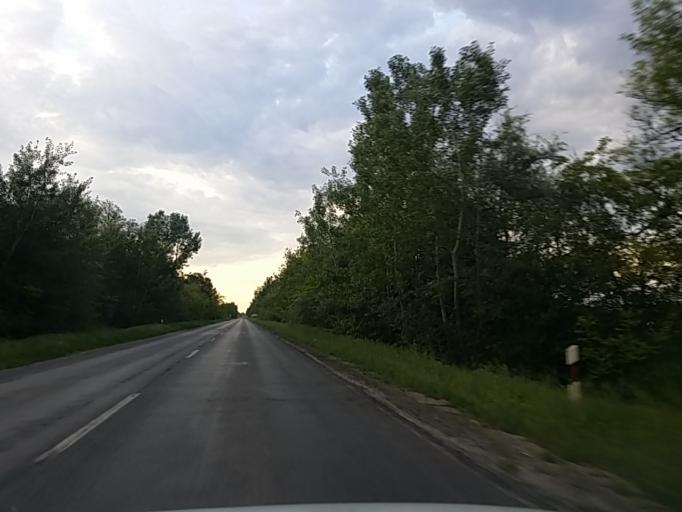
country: HU
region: Bacs-Kiskun
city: Lajosmizse
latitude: 47.0128
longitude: 19.5778
